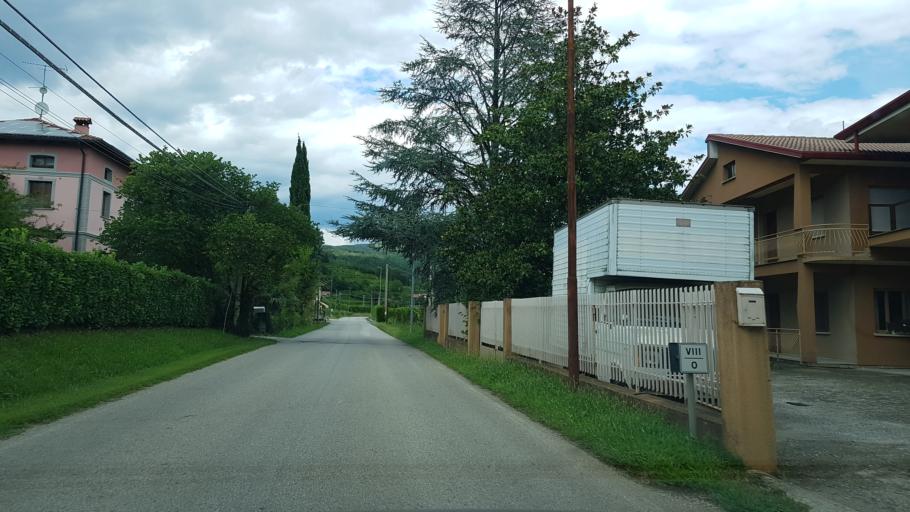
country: IT
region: Friuli Venezia Giulia
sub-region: Provincia di Udine
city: Prepotto
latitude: 46.0480
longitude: 13.4830
